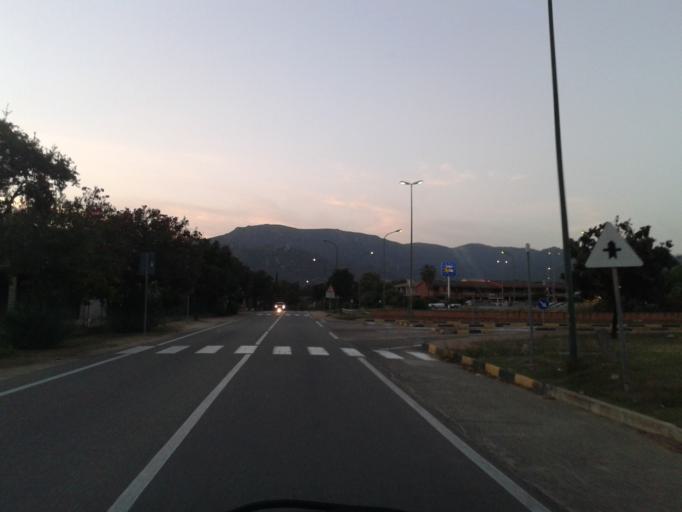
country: IT
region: Sardinia
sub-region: Provincia di Cagliari
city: Villasimius
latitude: 39.1481
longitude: 9.5148
